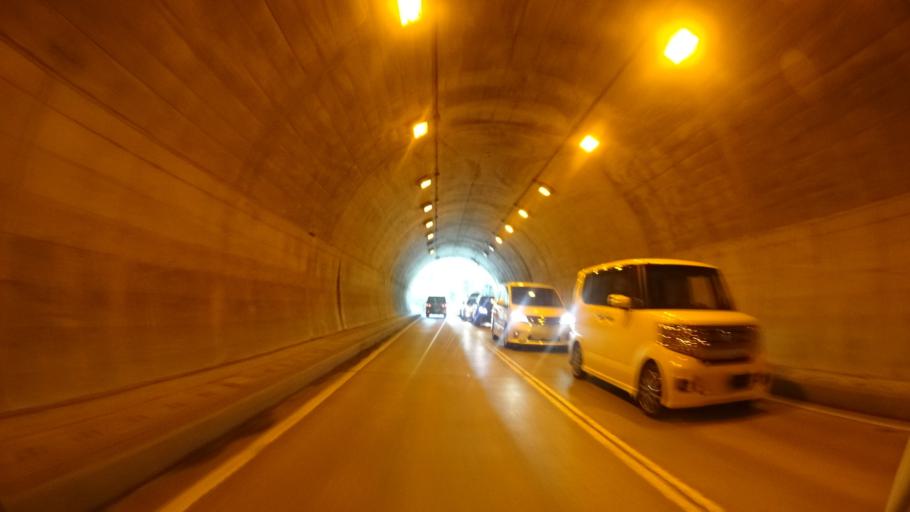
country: JP
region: Tokushima
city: Ikedacho
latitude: 33.8854
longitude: 133.8206
